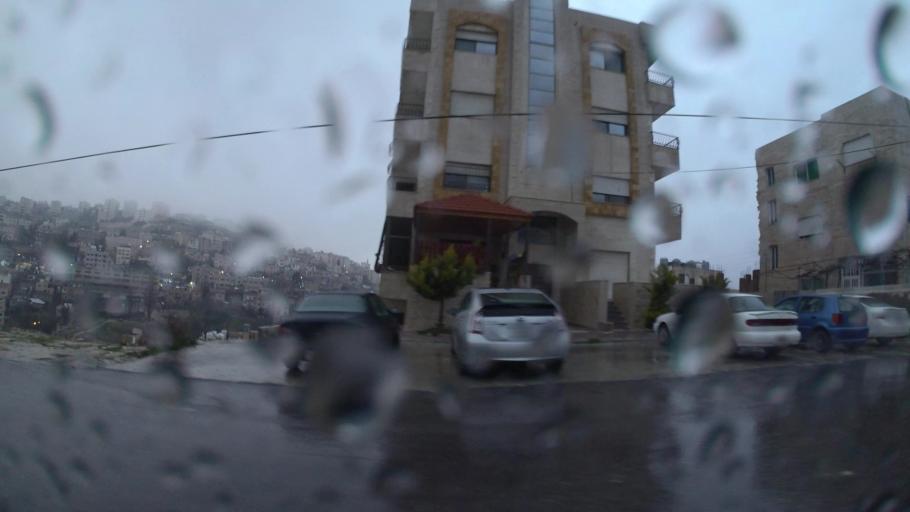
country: JO
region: Amman
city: Al Jubayhah
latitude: 32.0275
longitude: 35.8424
